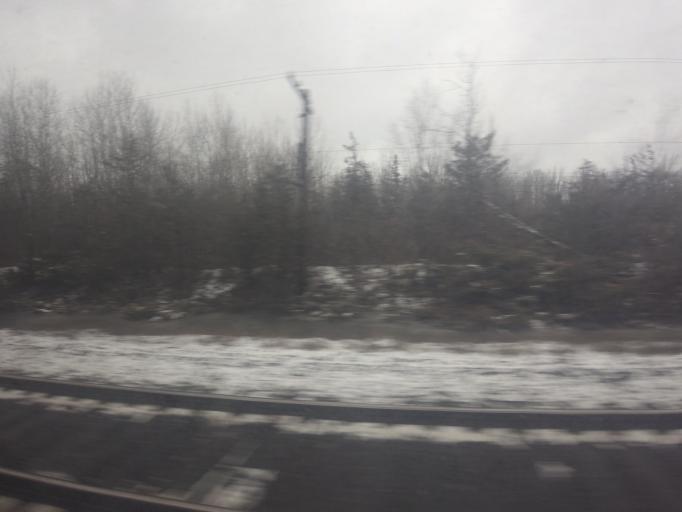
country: CA
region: Ontario
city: Quinte West
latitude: 44.1491
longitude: -77.4856
